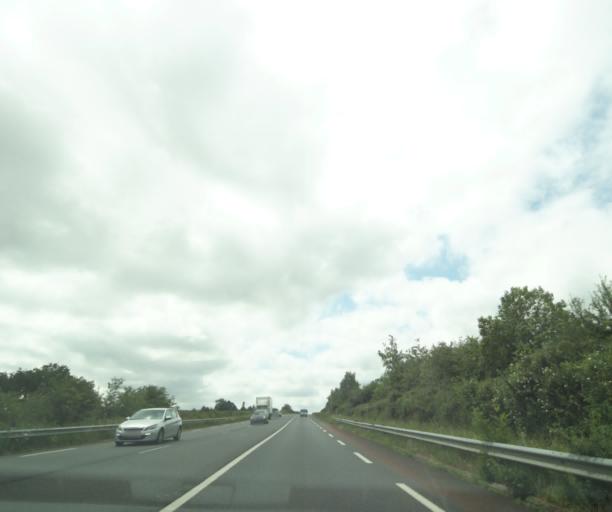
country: FR
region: Poitou-Charentes
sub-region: Departement des Deux-Sevres
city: Viennay
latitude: 46.7547
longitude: -0.2237
